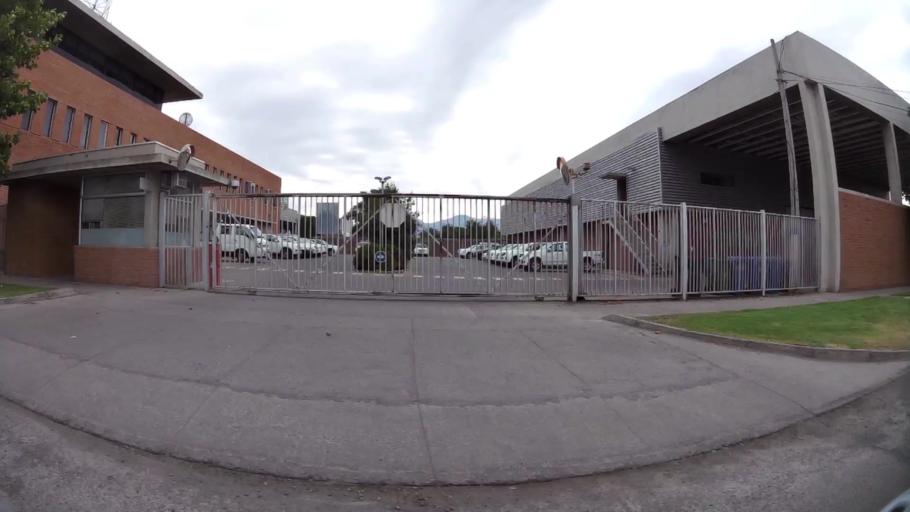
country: CL
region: O'Higgins
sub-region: Provincia de Cachapoal
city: Rancagua
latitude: -34.1660
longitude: -70.7302
